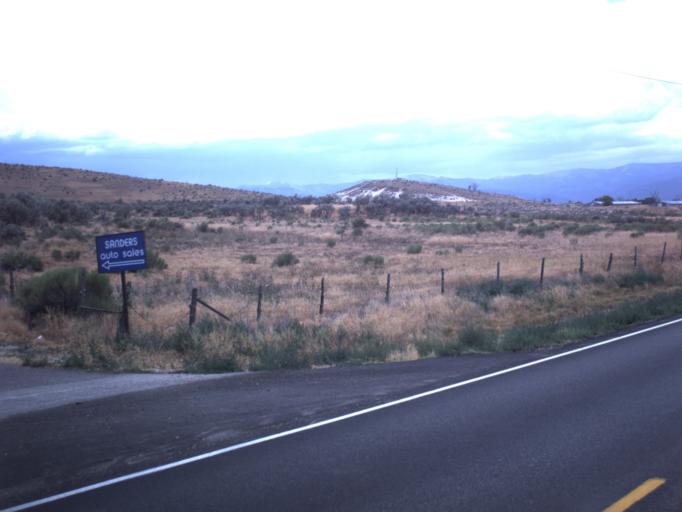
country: US
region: Utah
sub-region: Sanpete County
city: Moroni
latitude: 39.5397
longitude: -111.5948
